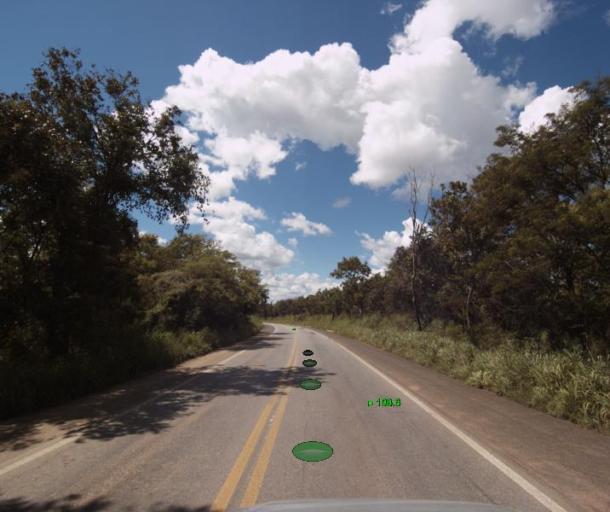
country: BR
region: Goias
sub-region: Porangatu
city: Porangatu
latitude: -13.7270
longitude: -49.0221
